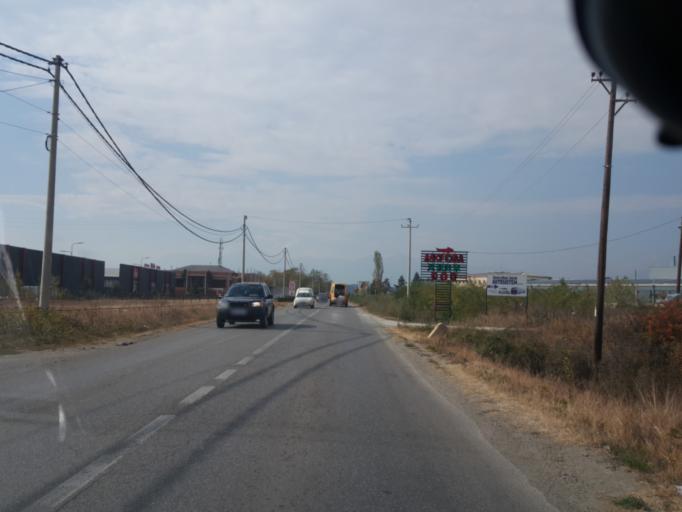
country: XK
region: Gjakova
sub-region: Komuna e Gjakoves
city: Gjakove
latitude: 42.3710
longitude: 20.4533
